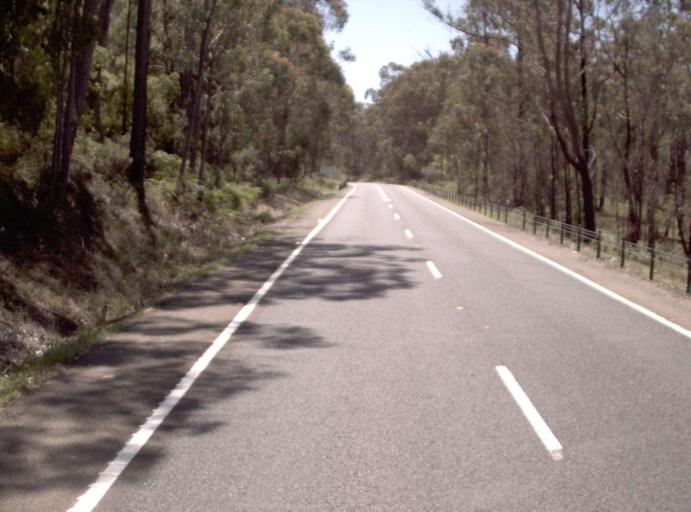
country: AU
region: Victoria
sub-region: East Gippsland
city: Lakes Entrance
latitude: -37.7878
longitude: 148.0534
